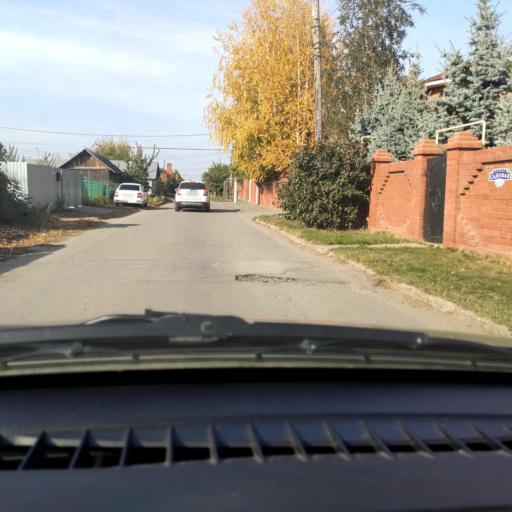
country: RU
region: Samara
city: Podstepki
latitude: 53.5142
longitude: 49.2323
